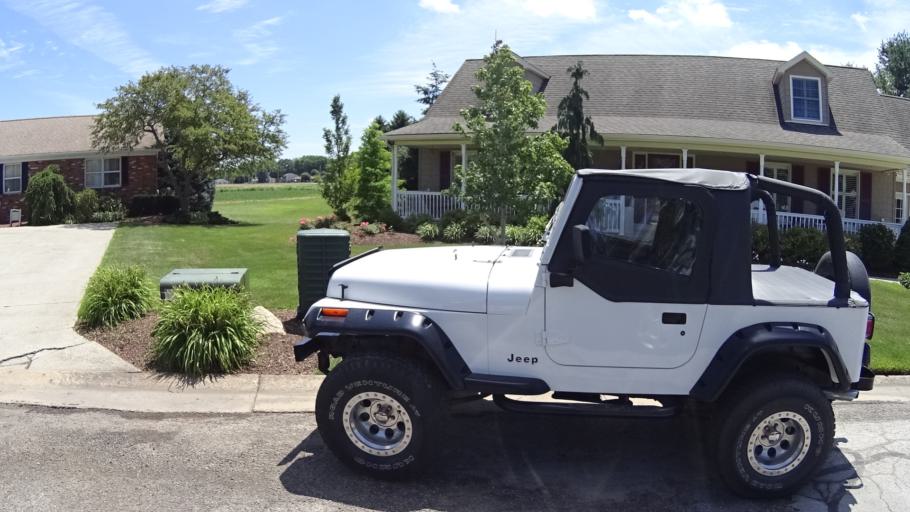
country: US
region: Ohio
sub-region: Erie County
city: Sandusky
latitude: 41.3972
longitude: -82.6867
